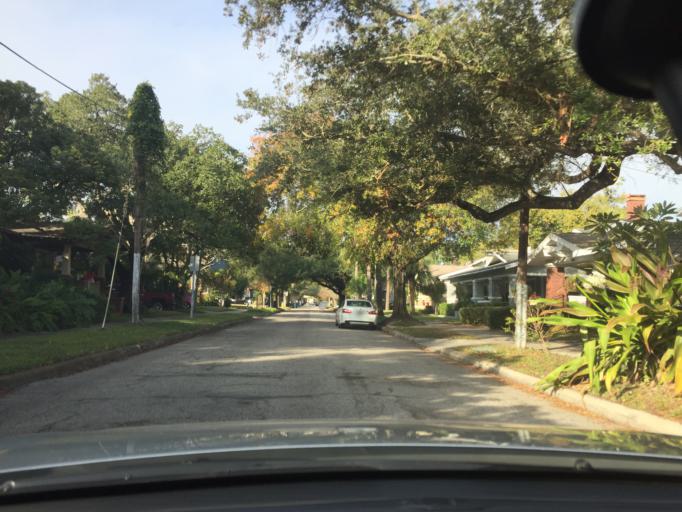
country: US
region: Florida
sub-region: Hillsborough County
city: Tampa
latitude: 27.9320
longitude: -82.4791
